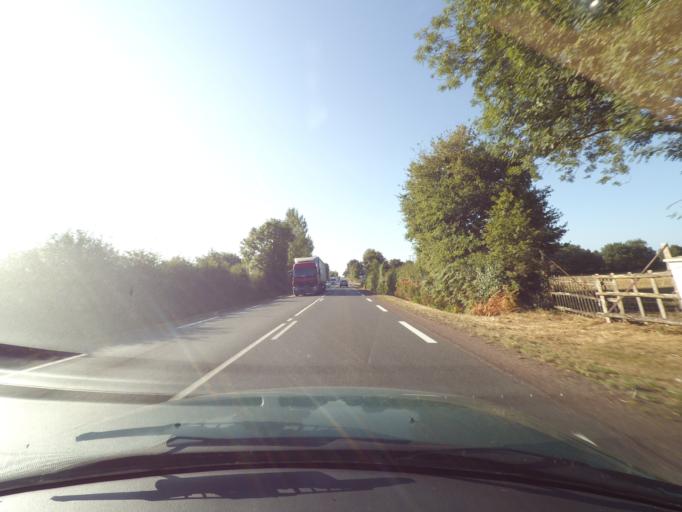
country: FR
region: Poitou-Charentes
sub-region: Departement des Deux-Sevres
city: Viennay
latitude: 46.6771
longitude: -0.2615
